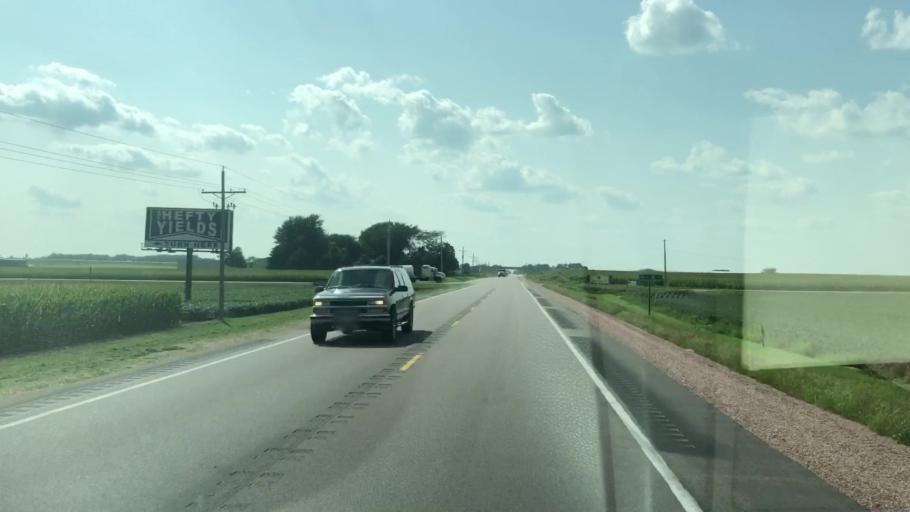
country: US
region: Iowa
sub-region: O'Brien County
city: Sheldon
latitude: 43.1861
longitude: -95.8003
